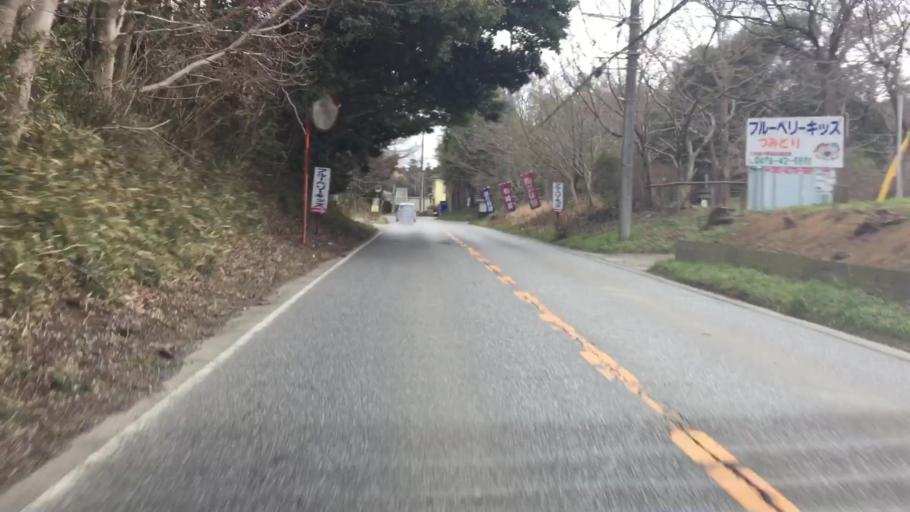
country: JP
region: Ibaraki
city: Ryugasaki
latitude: 35.8209
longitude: 140.1722
